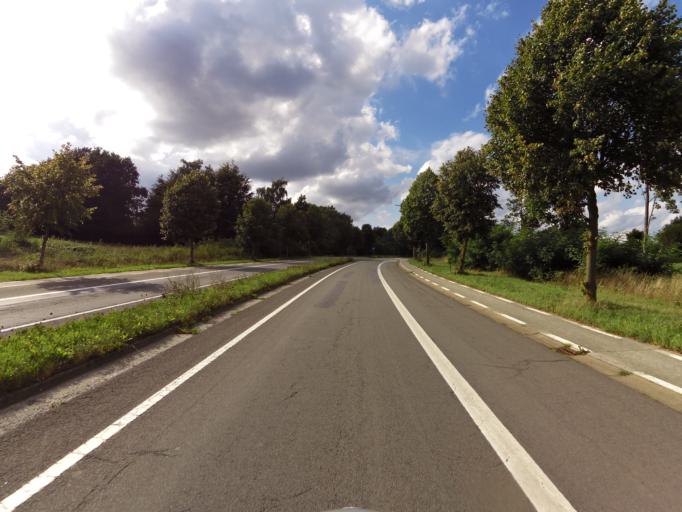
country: BE
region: Flanders
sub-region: Provincie Oost-Vlaanderen
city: Ronse
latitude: 50.7680
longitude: 3.5315
